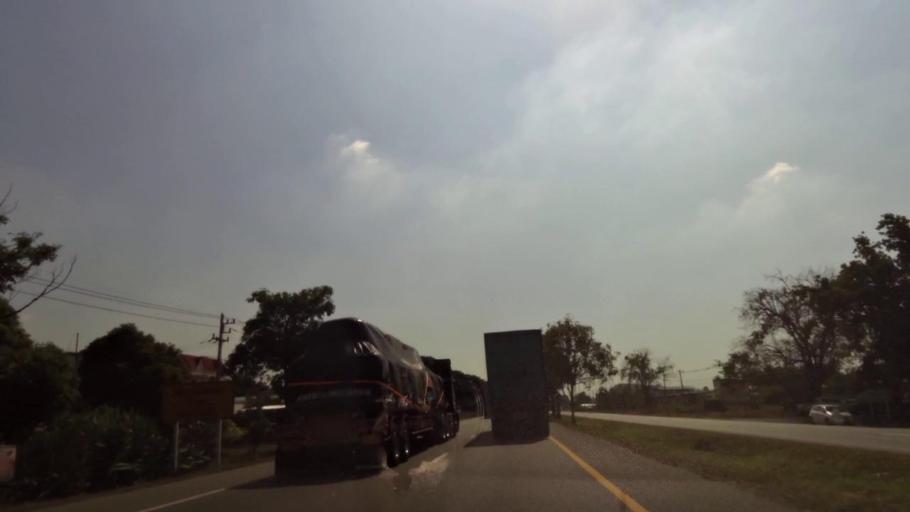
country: TH
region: Phichit
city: Bueng Na Rang
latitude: 16.1352
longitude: 100.1255
